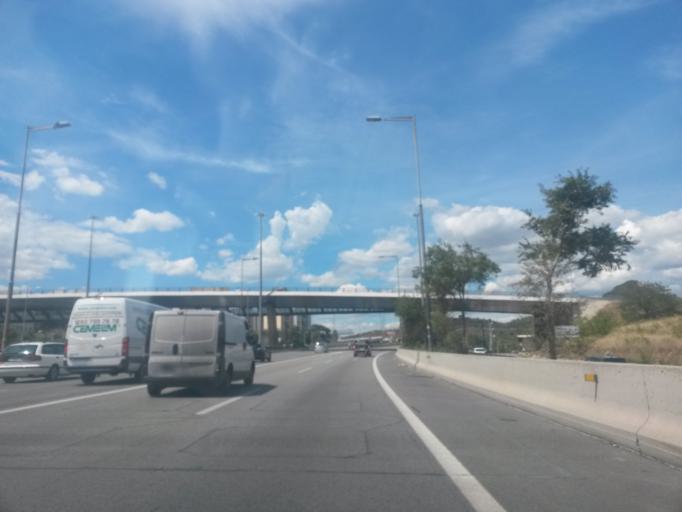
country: ES
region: Catalonia
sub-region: Provincia de Barcelona
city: Nou Barris
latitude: 41.4598
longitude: 2.1841
